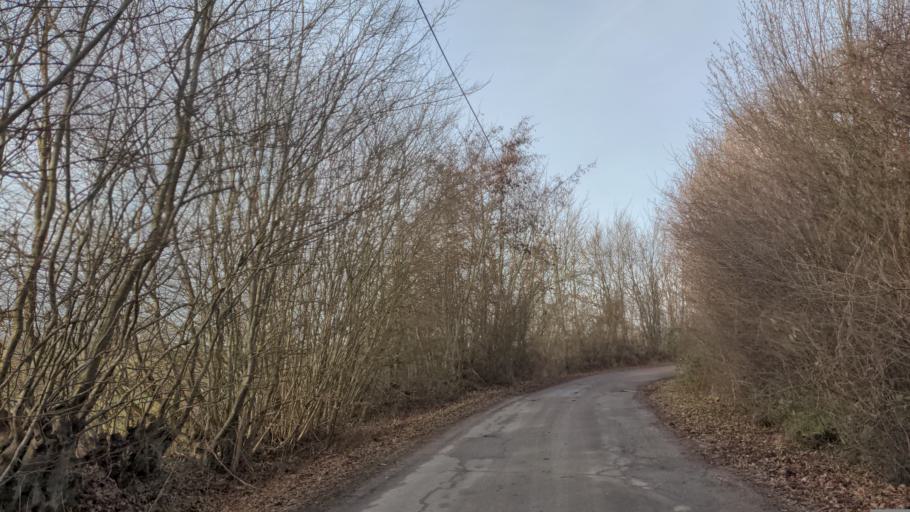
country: DE
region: Schleswig-Holstein
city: Eutin
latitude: 54.1679
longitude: 10.6258
